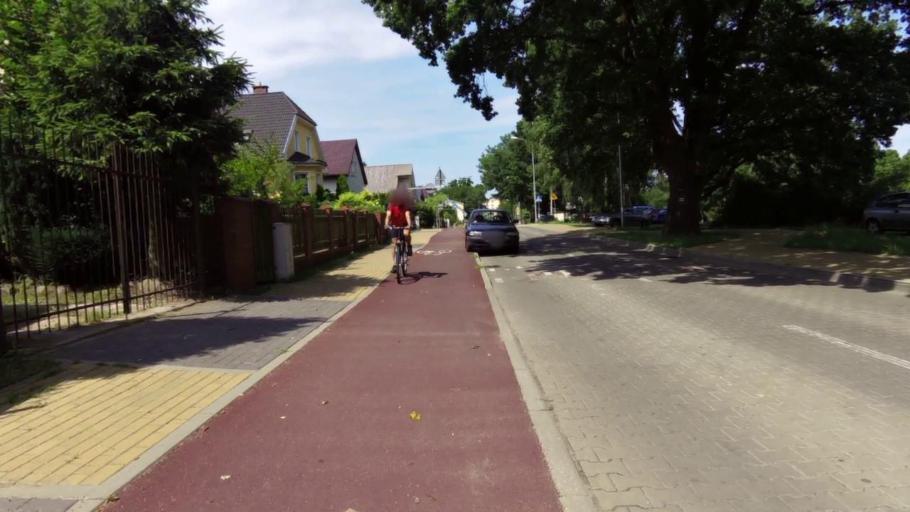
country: PL
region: West Pomeranian Voivodeship
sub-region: Powiat gryfinski
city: Stare Czarnowo
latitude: 53.3719
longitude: 14.6904
